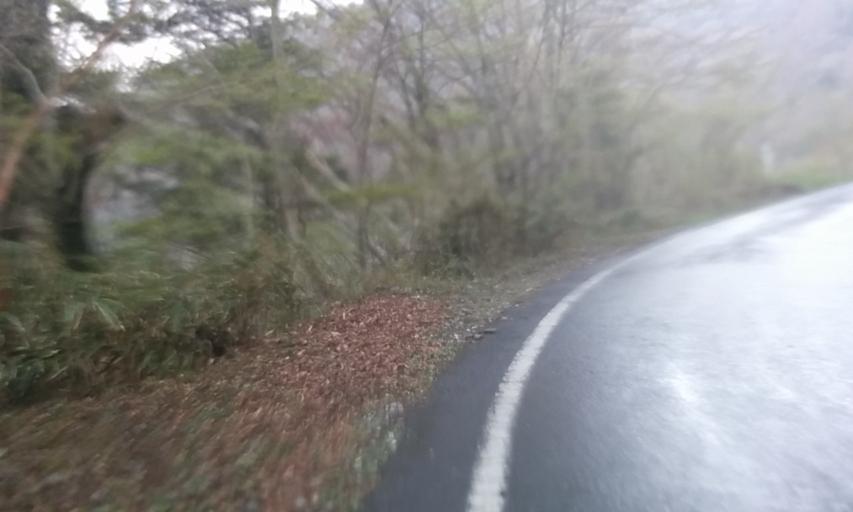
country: JP
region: Ehime
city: Saijo
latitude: 33.7839
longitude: 133.2783
